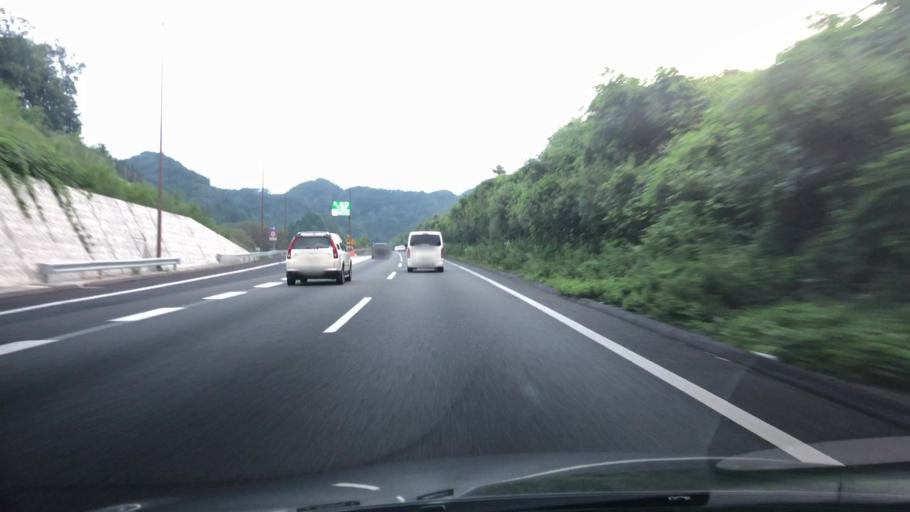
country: JP
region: Tokyo
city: Itsukaichi
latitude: 35.6823
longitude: 139.2538
